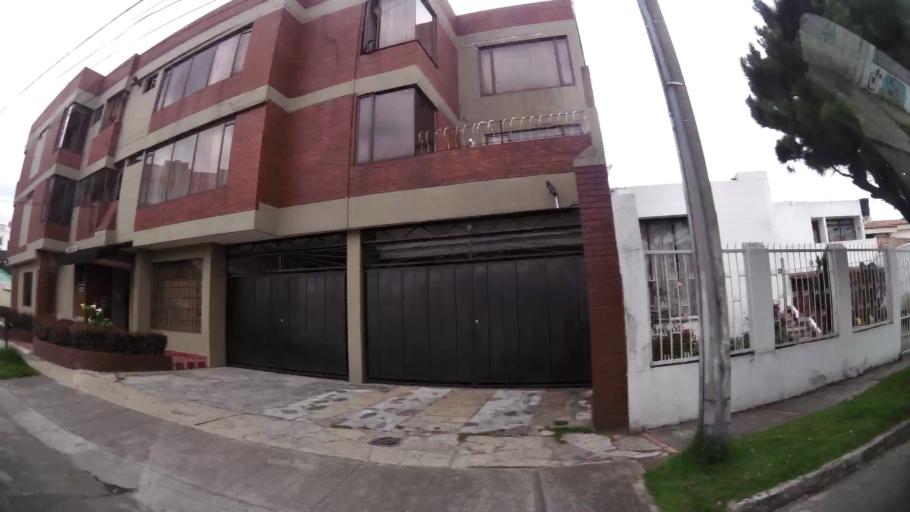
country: CO
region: Bogota D.C.
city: Barrio San Luis
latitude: 4.7155
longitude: -74.0714
